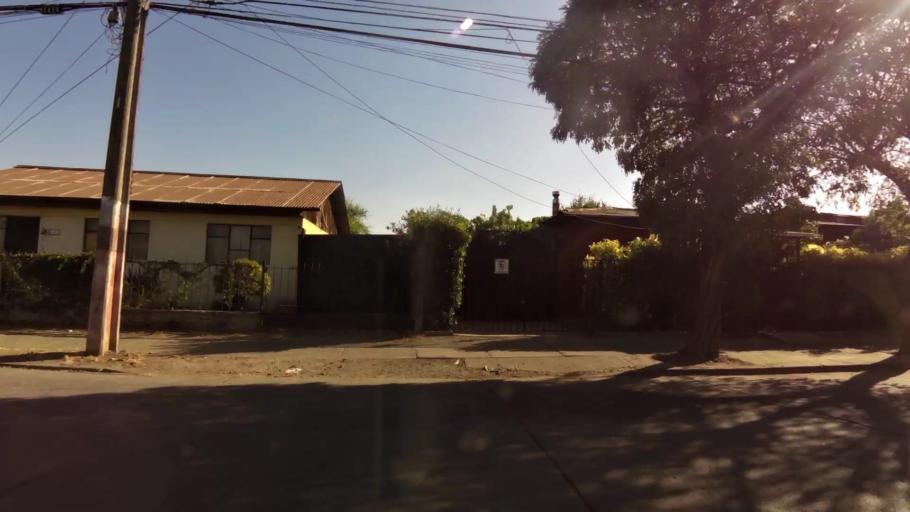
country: CL
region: Maule
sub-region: Provincia de Talca
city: Talca
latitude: -35.4436
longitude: -71.6664
